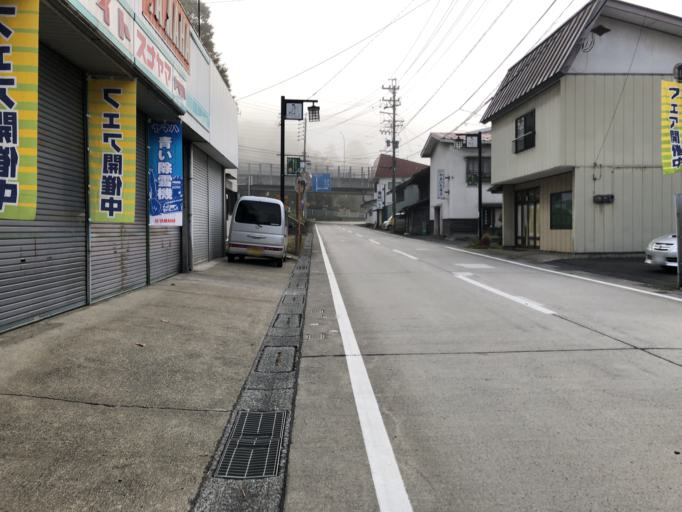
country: JP
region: Nagano
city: Nagano-shi
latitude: 36.8082
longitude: 138.1989
